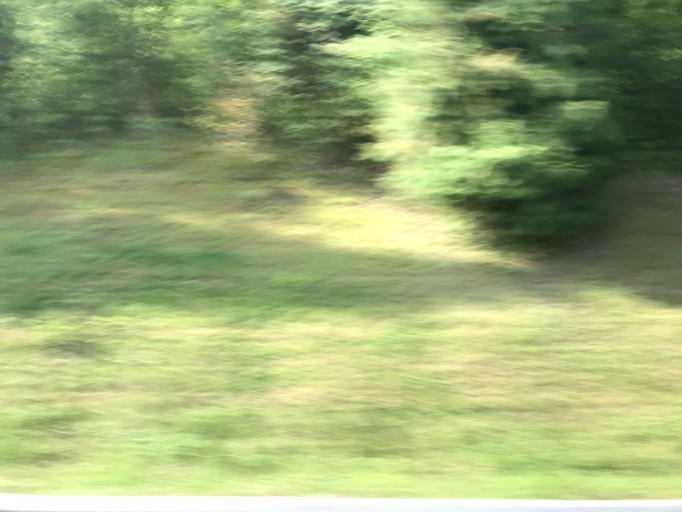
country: ES
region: Basque Country
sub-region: Provincia de Guipuzcoa
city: Legorreta
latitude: 43.0830
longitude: -2.1446
